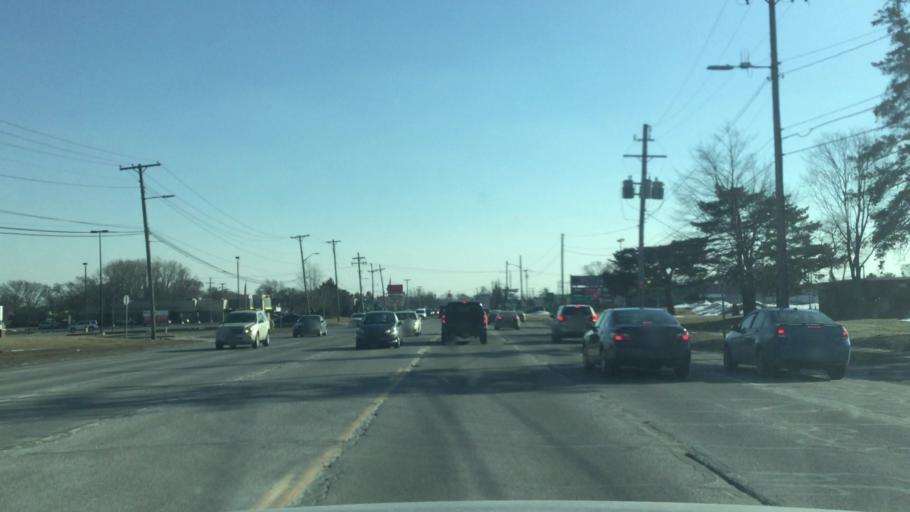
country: US
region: Michigan
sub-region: Wayne County
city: Westland
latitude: 42.3412
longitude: -83.3851
